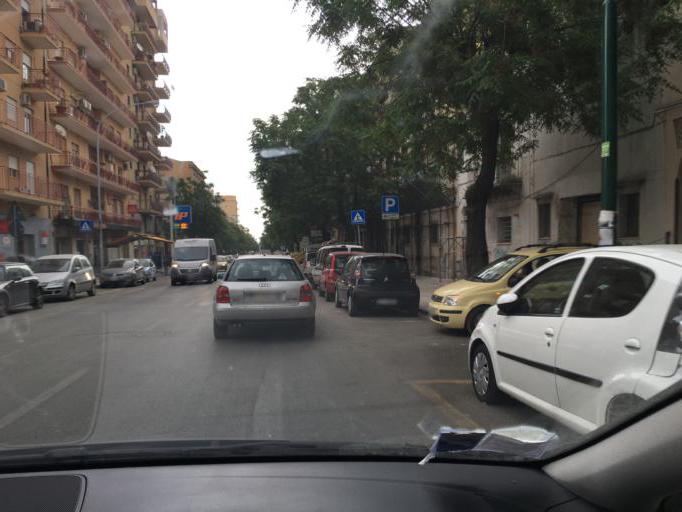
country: IT
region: Sicily
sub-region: Palermo
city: Palermo
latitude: 38.1059
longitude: 13.3374
